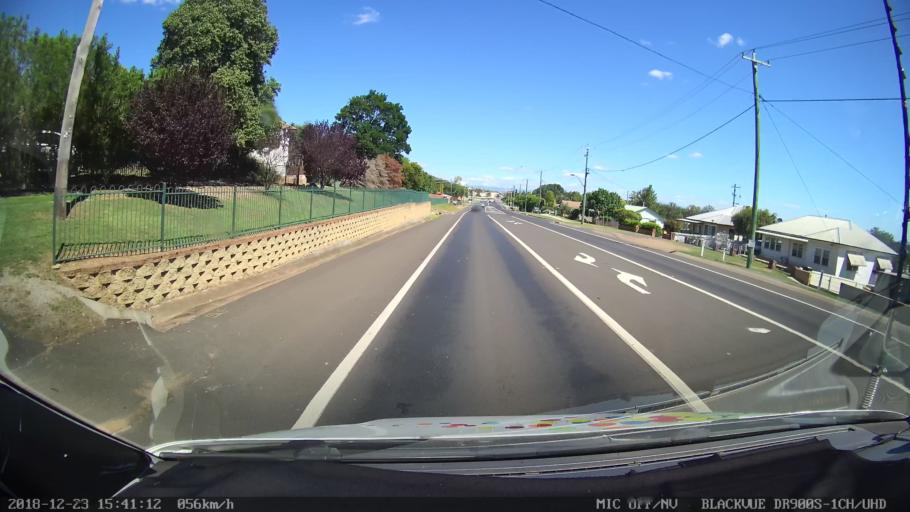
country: AU
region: New South Wales
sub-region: Tamworth Municipality
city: Tamworth
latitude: -31.0752
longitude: 150.9150
